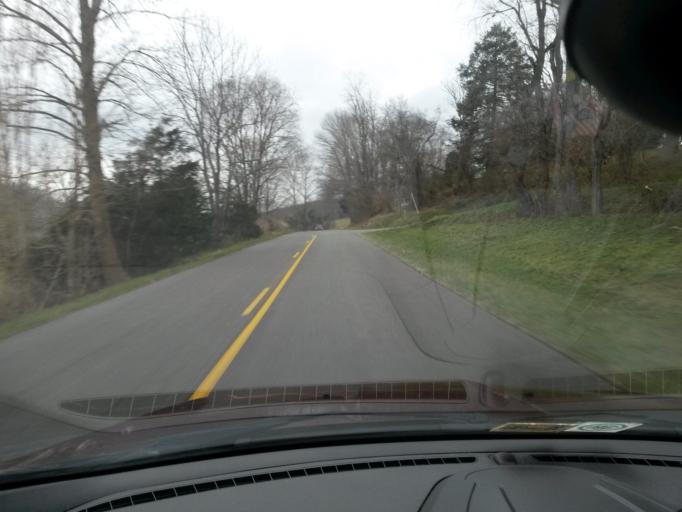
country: US
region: Virginia
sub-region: City of Lexington
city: Lexington
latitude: 37.8560
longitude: -79.4983
